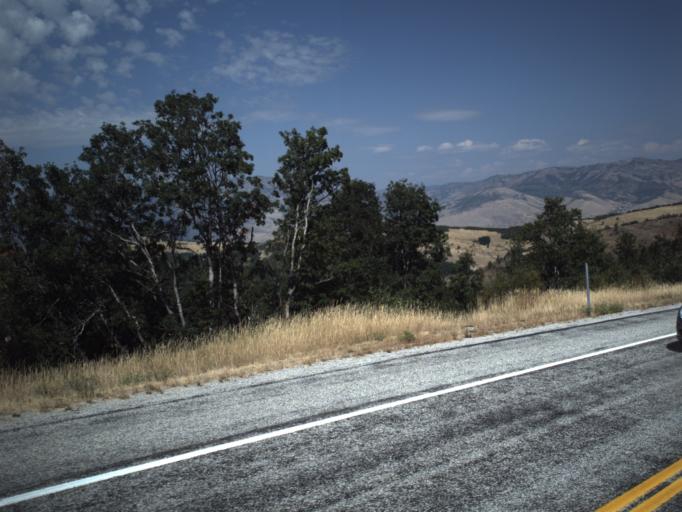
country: US
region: Utah
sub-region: Morgan County
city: Mountain Green
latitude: 41.2055
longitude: -111.8258
